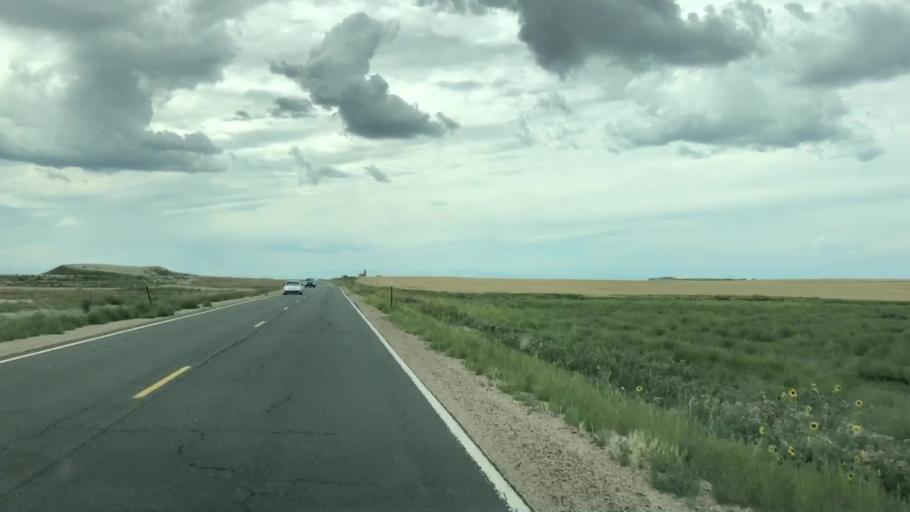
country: US
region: Colorado
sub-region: Adams County
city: Aurora
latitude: 39.7985
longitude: -104.6947
